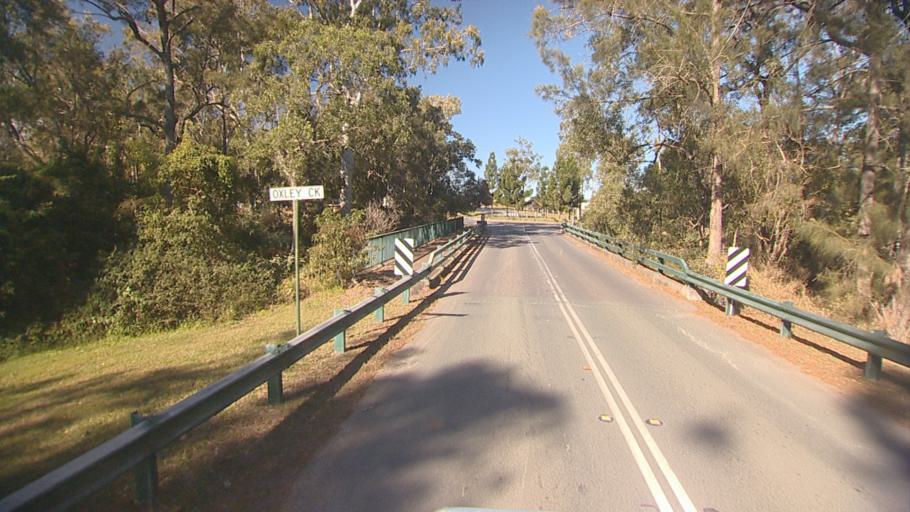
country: AU
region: Queensland
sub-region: Ipswich
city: Springfield Lakes
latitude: -27.7326
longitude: 152.9461
